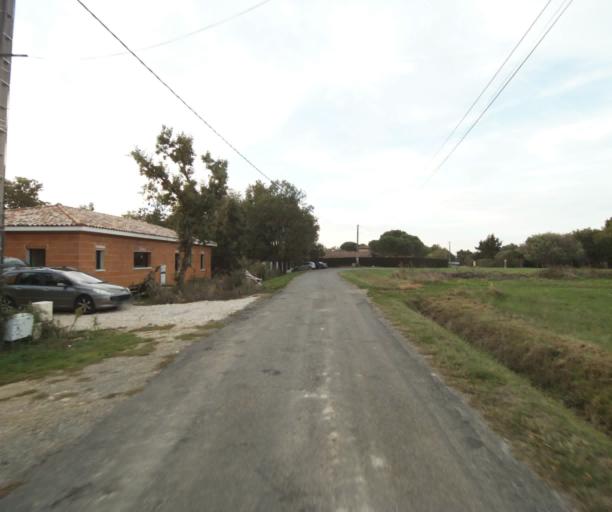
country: FR
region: Midi-Pyrenees
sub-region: Departement du Tarn-et-Garonne
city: Pompignan
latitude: 43.8239
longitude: 1.3146
